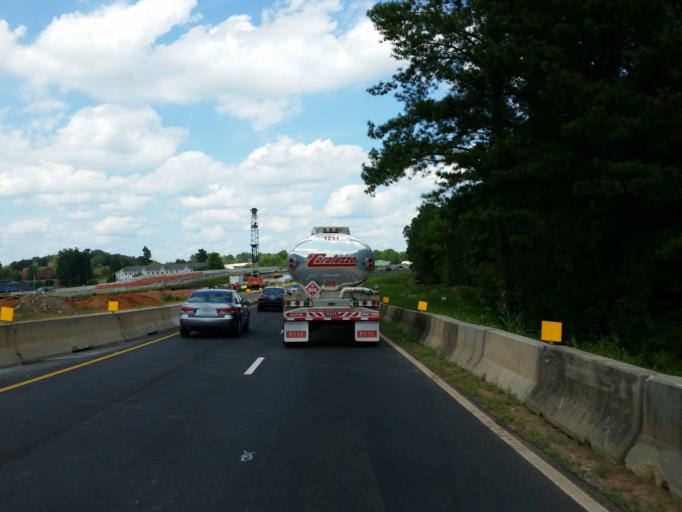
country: US
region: Georgia
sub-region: Gwinnett County
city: Lawrenceville
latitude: 33.9740
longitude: -84.0055
